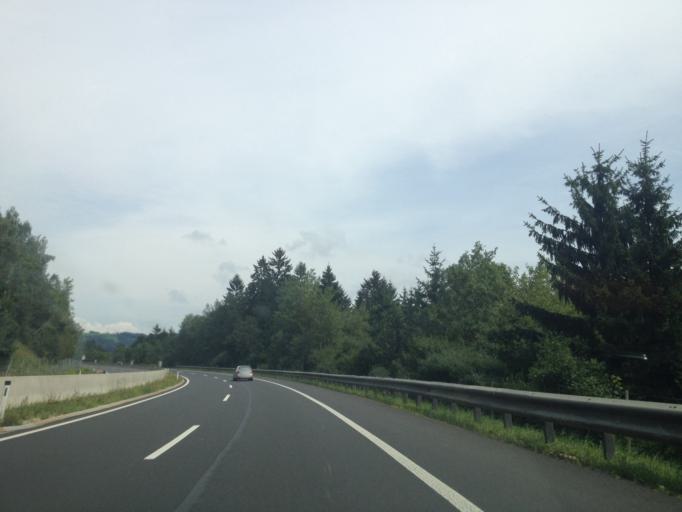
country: AT
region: Styria
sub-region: Politischer Bezirk Hartberg-Fuerstenfeld
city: Pinggau
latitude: 47.4231
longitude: 16.0957
